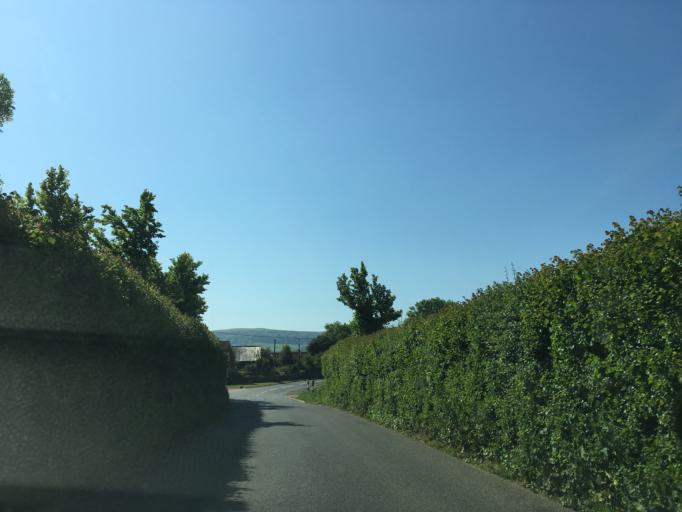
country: GB
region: England
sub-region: Isle of Wight
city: Newchurch
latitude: 50.6441
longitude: -1.2098
